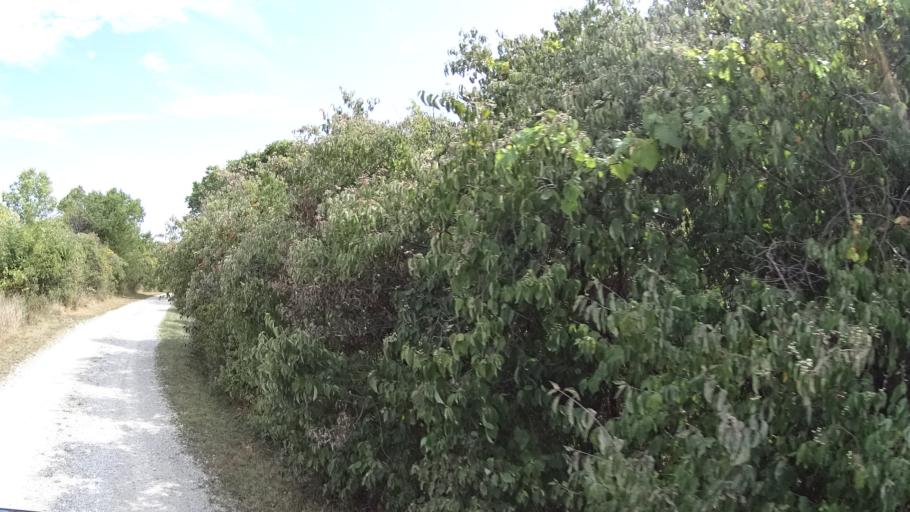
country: US
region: Ohio
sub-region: Erie County
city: Sandusky
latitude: 41.5935
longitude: -82.6849
